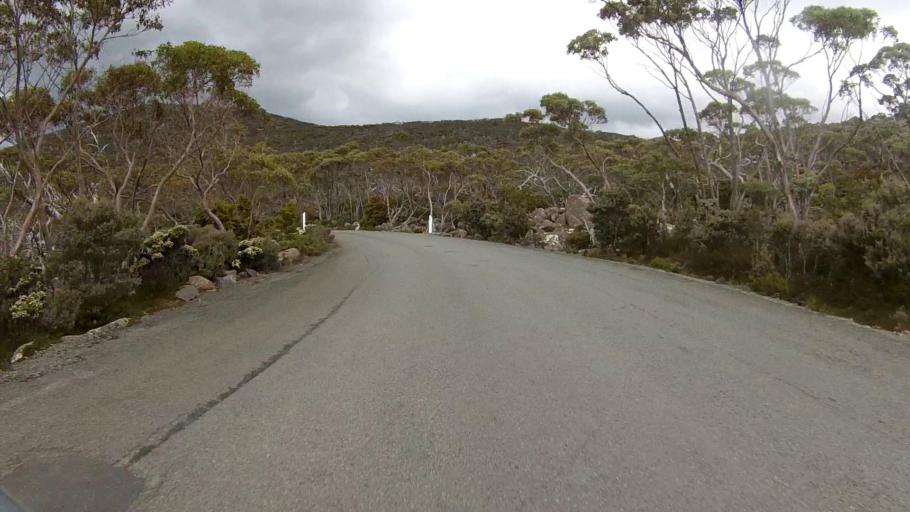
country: AU
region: Tasmania
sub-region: Glenorchy
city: West Moonah
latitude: -42.8861
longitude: 147.2222
